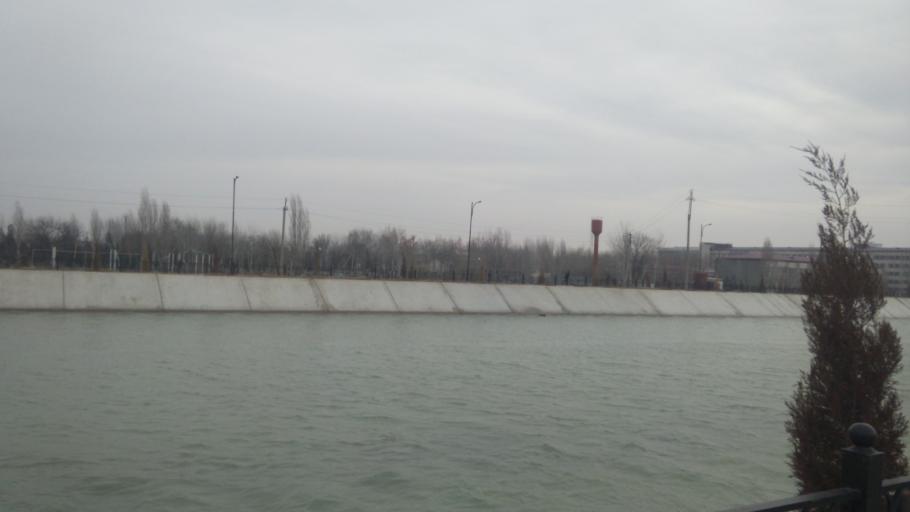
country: UZ
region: Sirdaryo
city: Guliston
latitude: 40.5054
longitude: 68.7809
